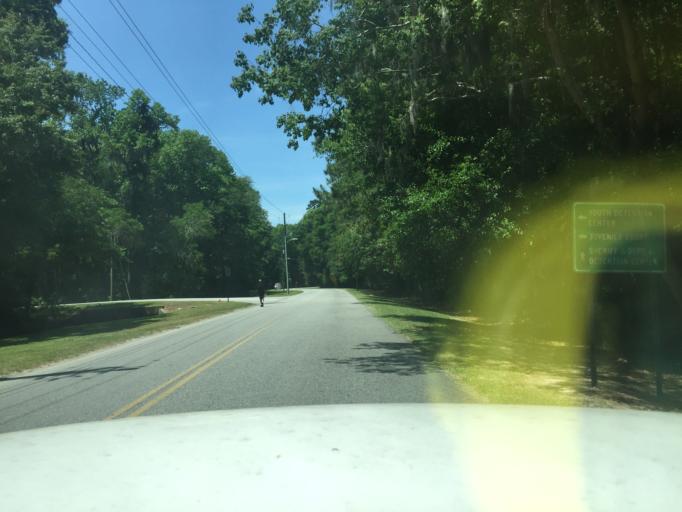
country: US
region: Georgia
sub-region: Chatham County
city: Garden City
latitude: 32.0625
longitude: -81.1645
